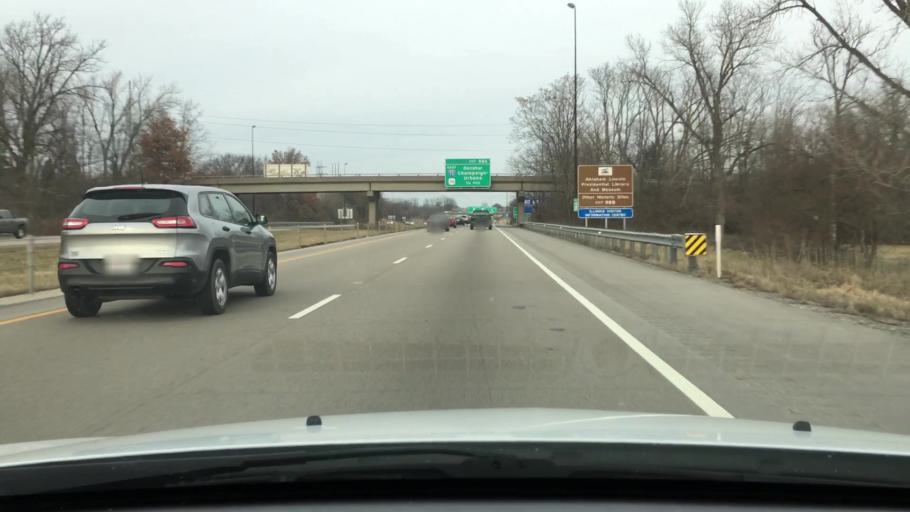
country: US
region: Illinois
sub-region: Sangamon County
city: Grandview
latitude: 39.7936
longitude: -89.5973
